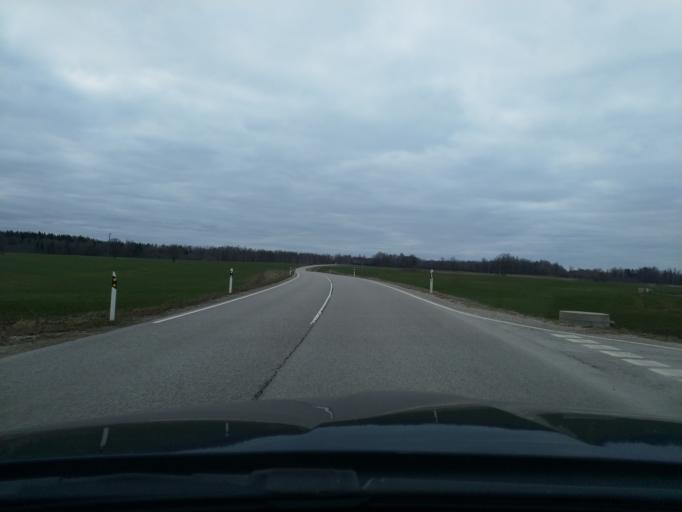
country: LV
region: Talsu Rajons
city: Sabile
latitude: 56.9420
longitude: 22.4899
